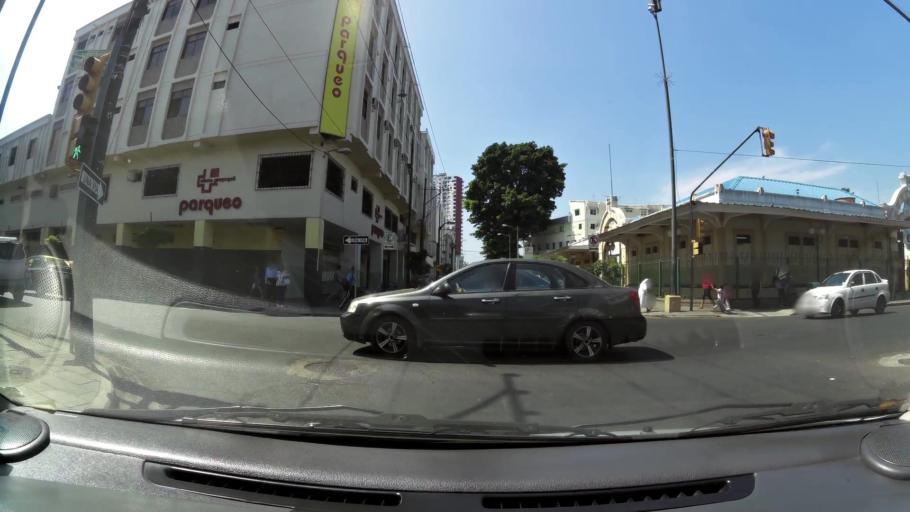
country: EC
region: Guayas
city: Eloy Alfaro
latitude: -2.1856
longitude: -79.8809
